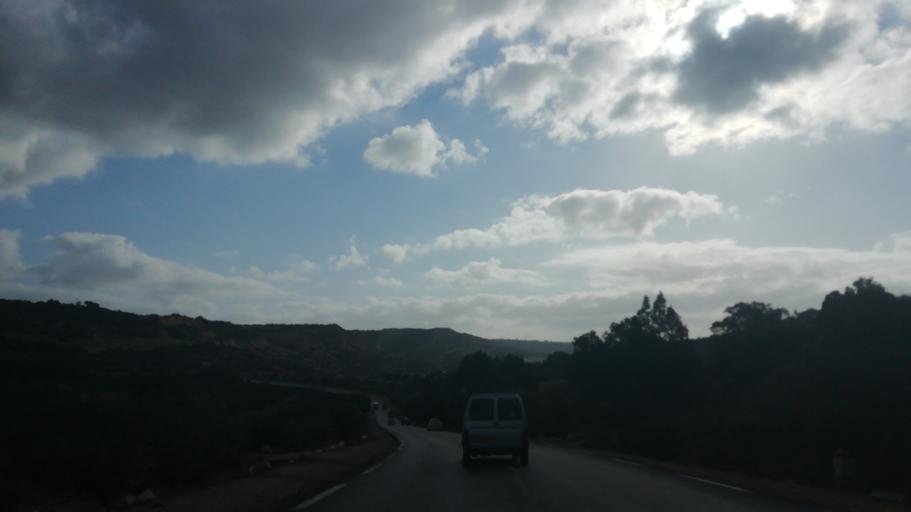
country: DZ
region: Relizane
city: Mazouna
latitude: 36.2378
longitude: 0.5374
